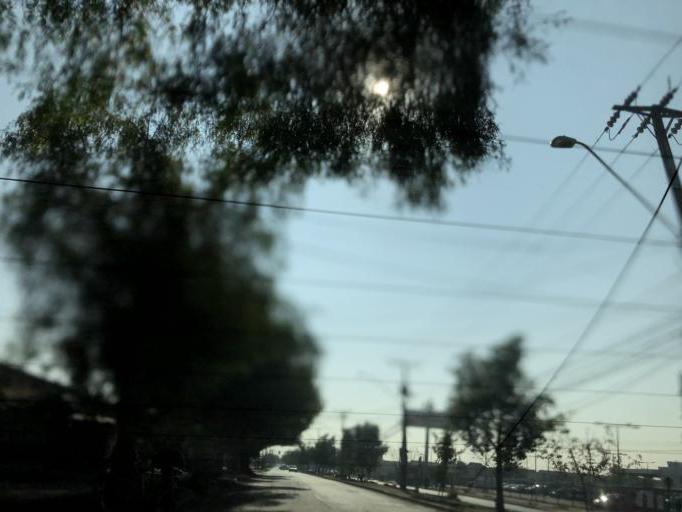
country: CL
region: Santiago Metropolitan
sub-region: Provincia de Cordillera
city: Puente Alto
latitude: -33.5936
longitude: -70.5597
